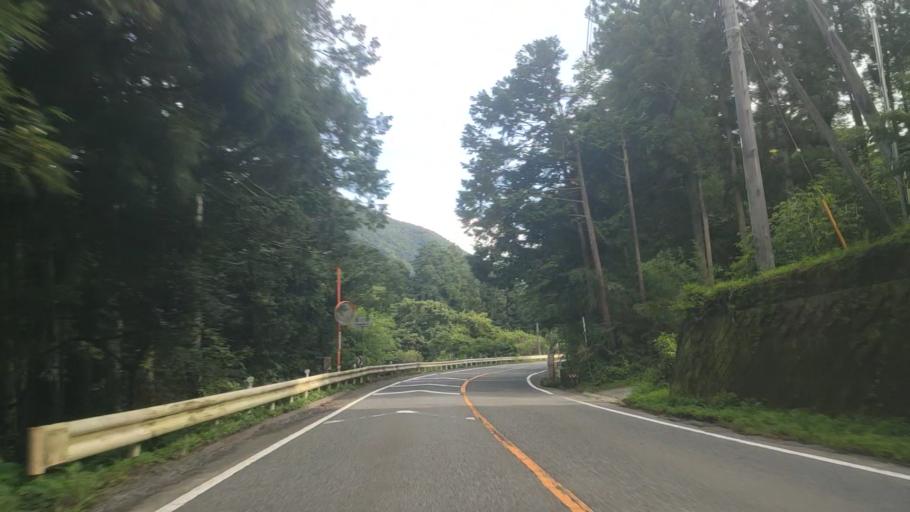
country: JP
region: Gunma
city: Omamacho-omama
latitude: 36.5174
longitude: 139.3029
